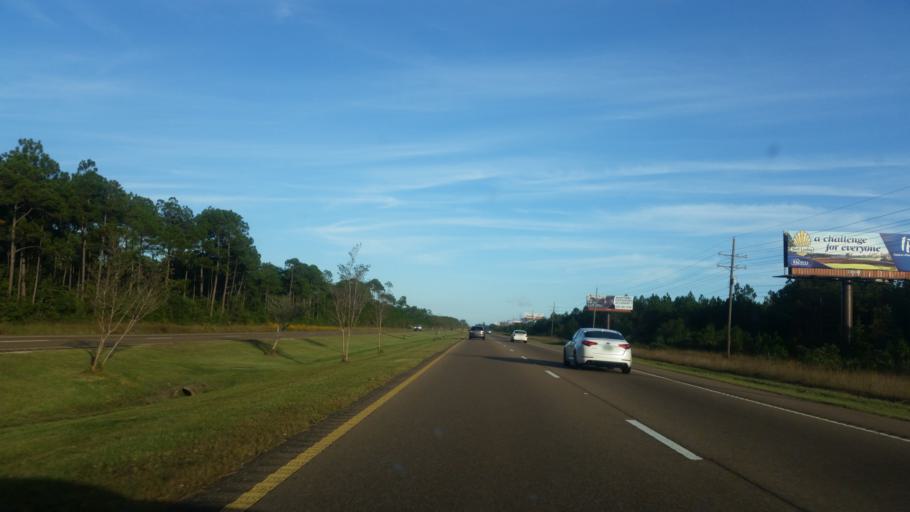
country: US
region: Mississippi
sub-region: Jackson County
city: Gulf Park Estates
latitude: 30.4014
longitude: -88.7133
